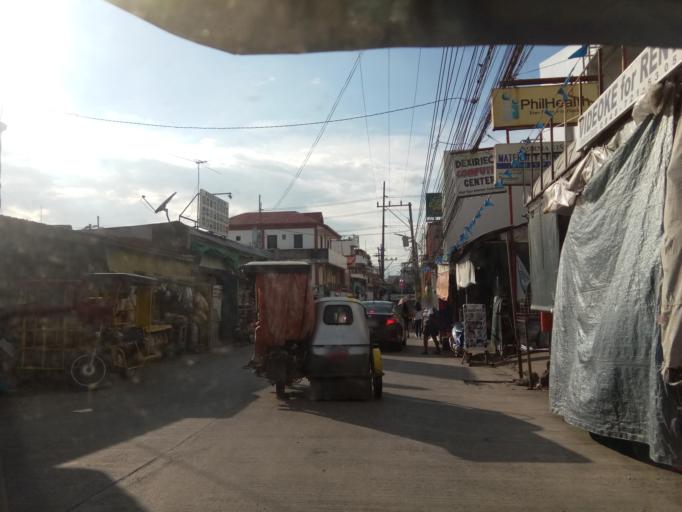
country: PH
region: Calabarzon
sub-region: Province of Cavite
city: Dasmarinas
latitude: 14.2929
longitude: 120.9390
